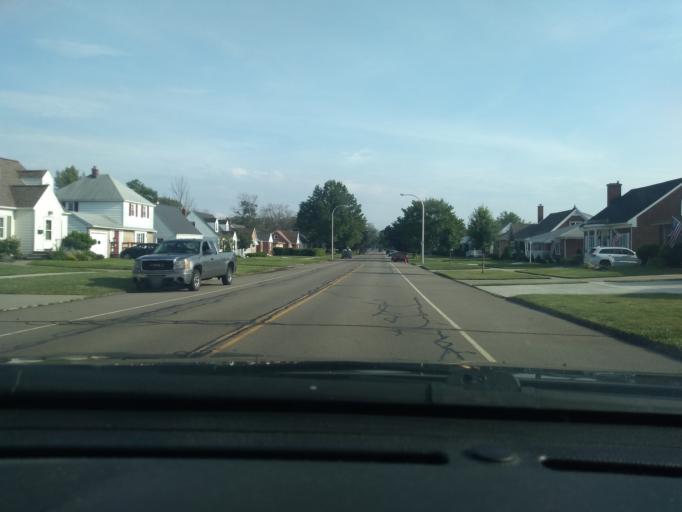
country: US
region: New York
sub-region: Erie County
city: Lackawanna
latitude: 42.8251
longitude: -78.8100
